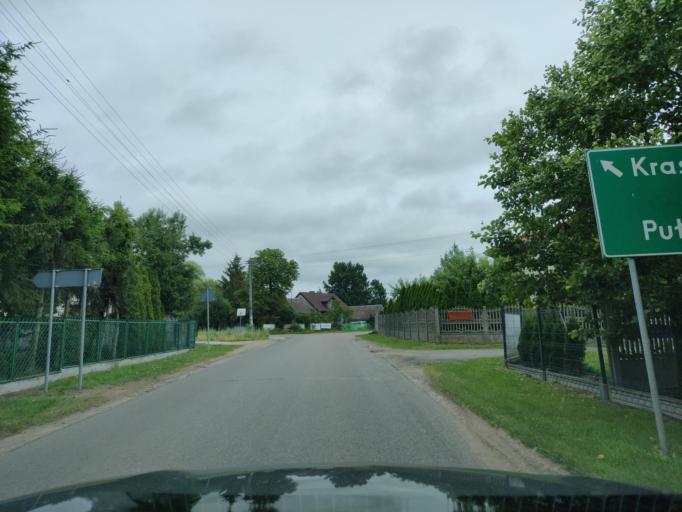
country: PL
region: Masovian Voivodeship
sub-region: Powiat przasnyski
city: Krasne
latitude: 52.9232
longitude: 20.9334
